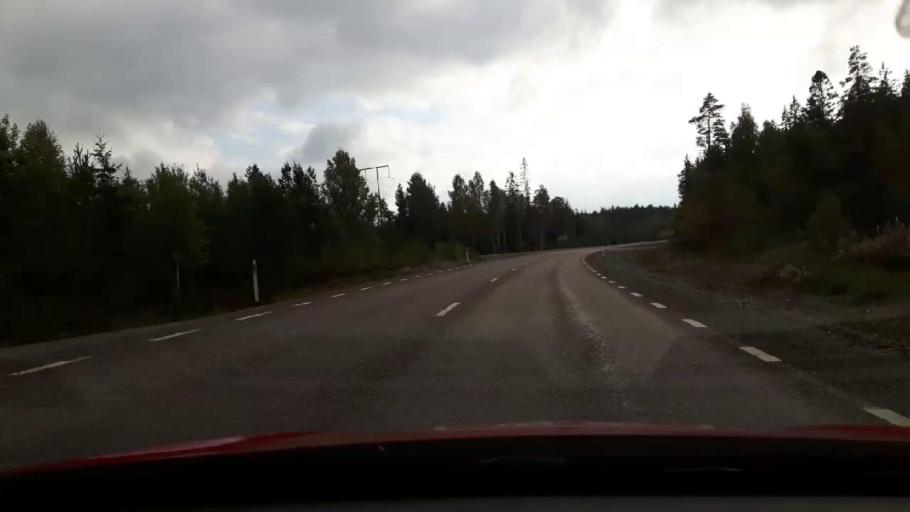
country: SE
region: Gaevleborg
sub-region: Soderhamns Kommun
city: Ljusne
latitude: 61.0973
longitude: 16.9530
